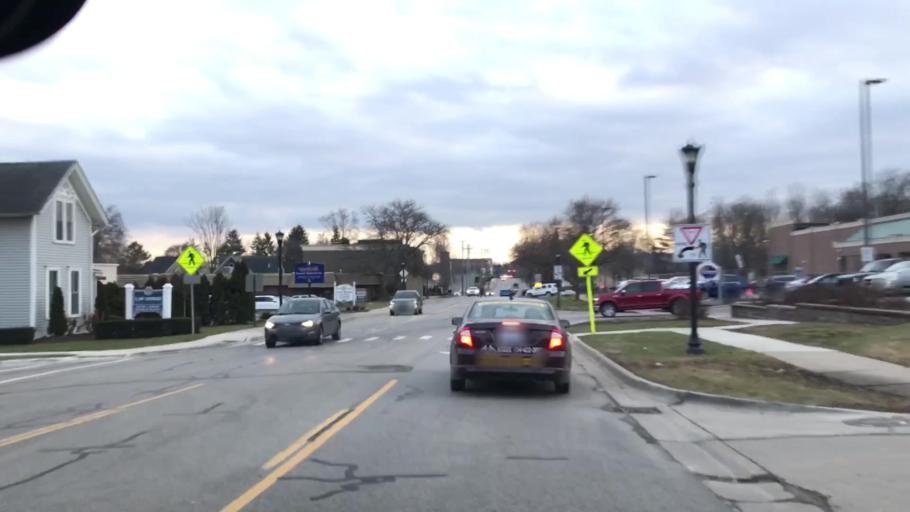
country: US
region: Michigan
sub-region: Wayne County
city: Northville
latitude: 42.4360
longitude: -83.4832
